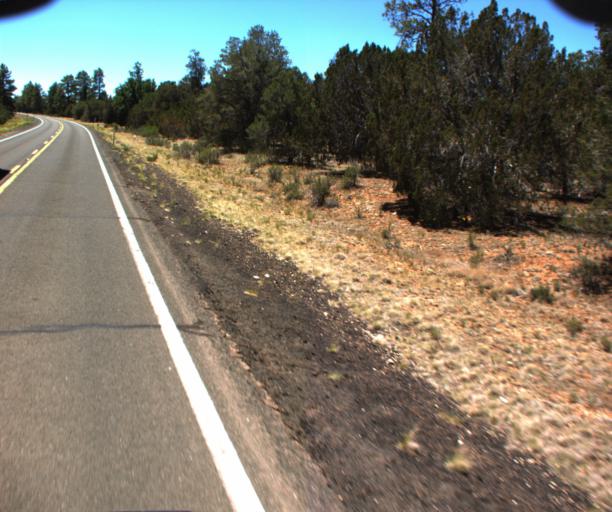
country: US
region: Arizona
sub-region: Gila County
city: Star Valley
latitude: 34.6868
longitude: -111.1122
